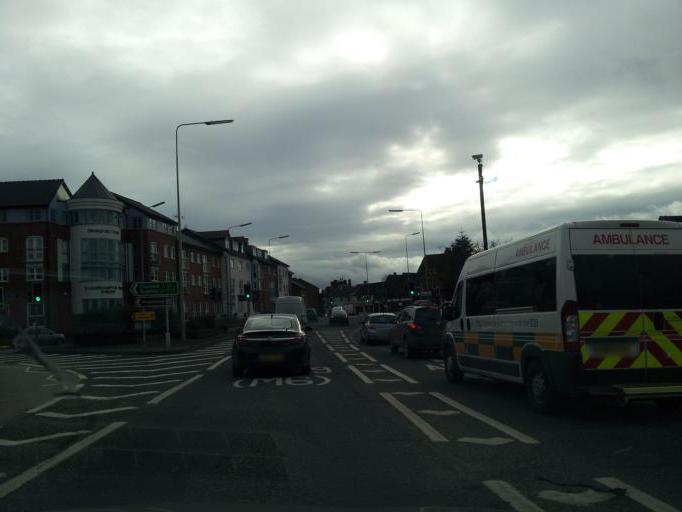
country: GB
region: England
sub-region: Staffordshire
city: Stafford
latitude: 52.8032
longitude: -2.1125
